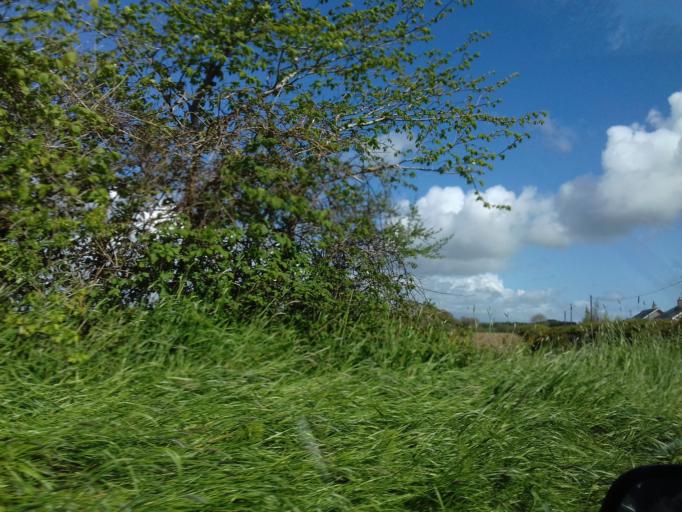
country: IE
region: Leinster
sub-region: Loch Garman
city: Castlebridge
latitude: 52.3891
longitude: -6.4076
